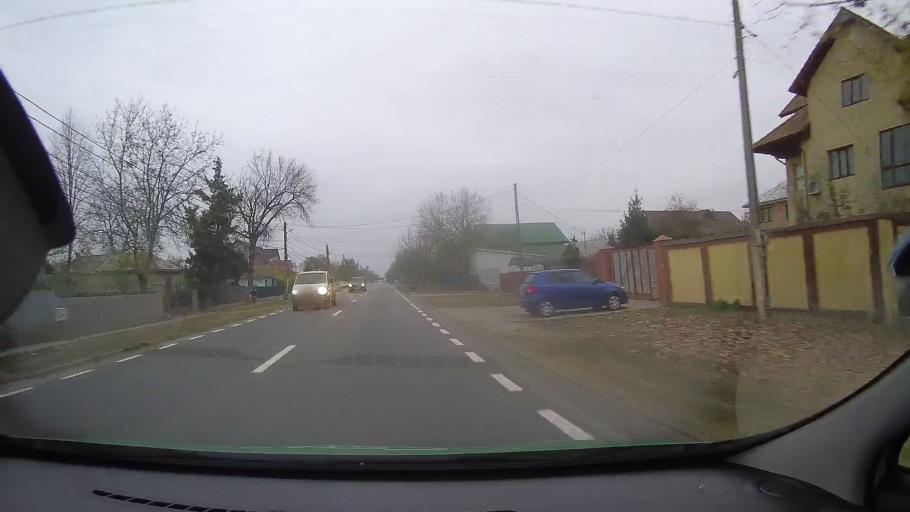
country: RO
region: Ialomita
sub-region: Comuna Slobozia
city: Slobozia
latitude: 44.6009
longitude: 27.3883
